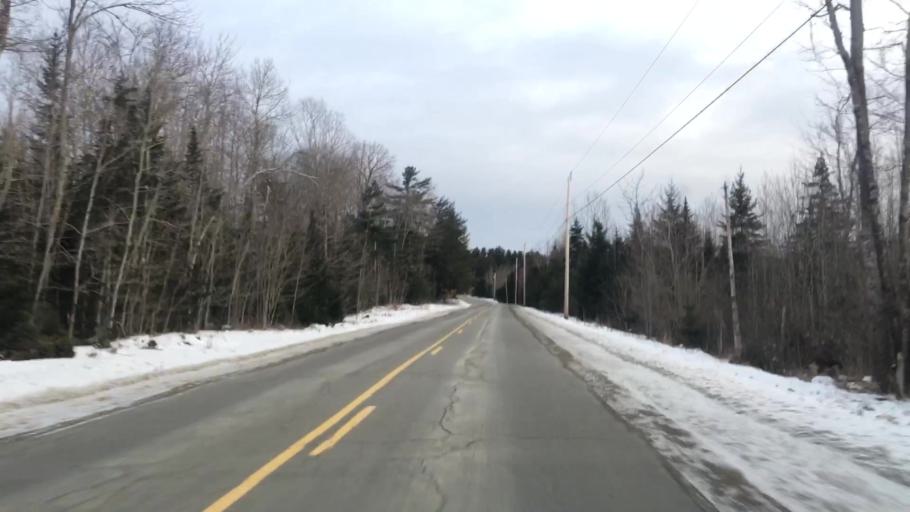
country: US
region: Maine
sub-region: Hancock County
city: Franklin
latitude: 44.7602
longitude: -68.3250
